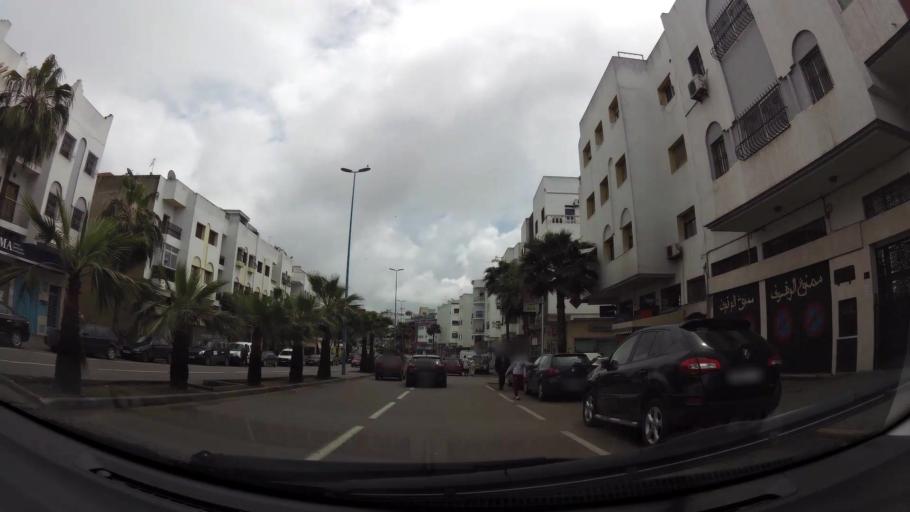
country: MA
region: Grand Casablanca
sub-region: Casablanca
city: Casablanca
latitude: 33.5405
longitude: -7.6830
